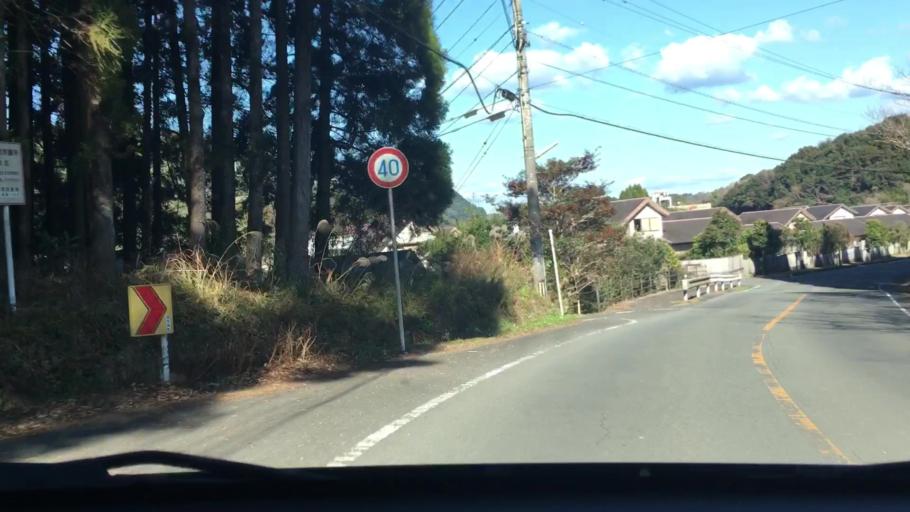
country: JP
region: Kagoshima
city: Satsumasendai
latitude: 31.7817
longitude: 130.3992
